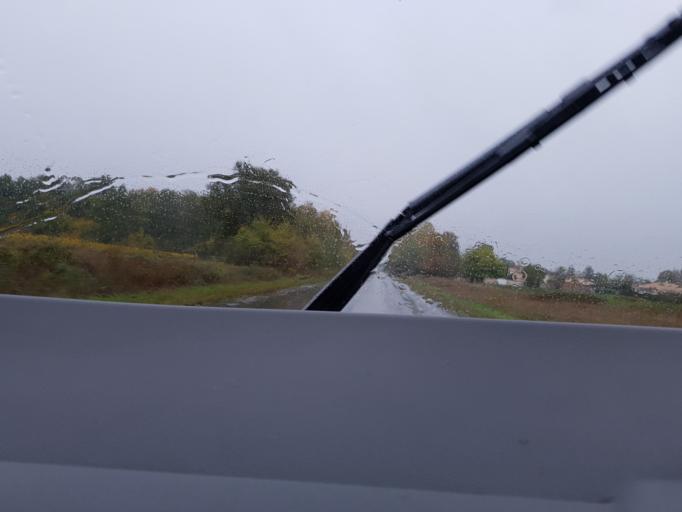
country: FR
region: Aquitaine
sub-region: Departement de la Gironde
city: Saint-Louis-de-Montferrand
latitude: 44.9606
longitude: -0.5088
